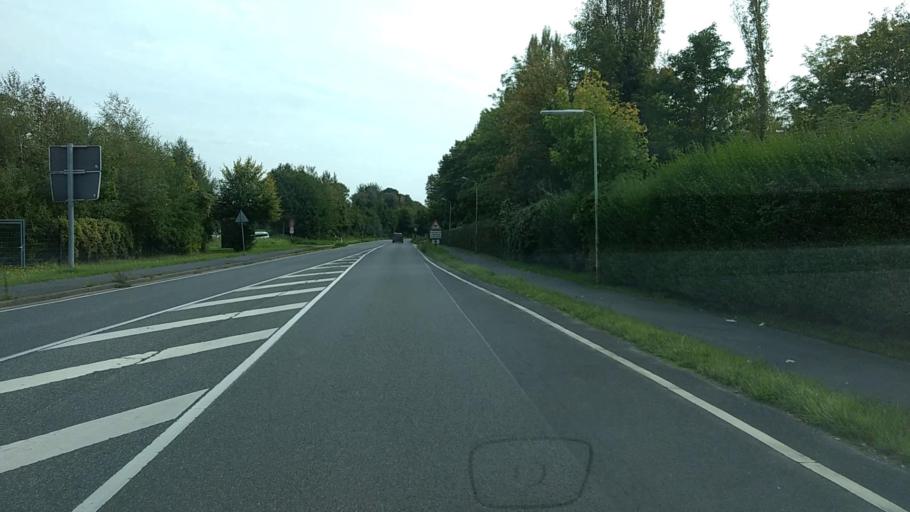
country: DE
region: North Rhine-Westphalia
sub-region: Regierungsbezirk Koln
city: Bergheim
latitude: 50.9484
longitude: 6.6610
